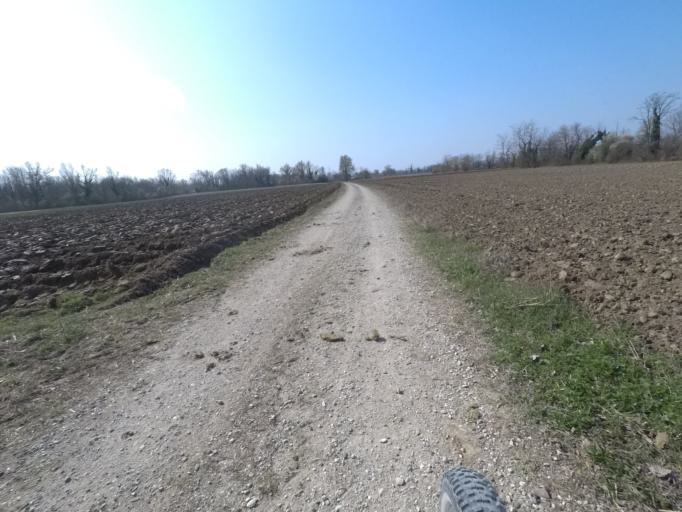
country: IT
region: Friuli Venezia Giulia
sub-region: Provincia di Udine
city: Remanzacco
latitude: 46.0670
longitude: 13.3304
